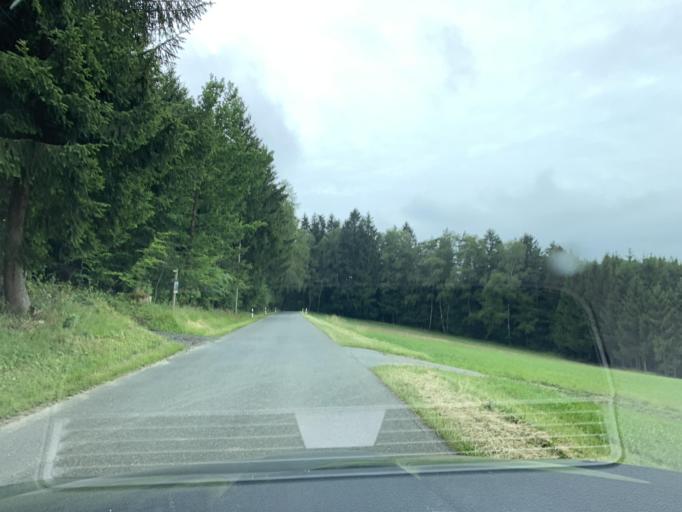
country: DE
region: Bavaria
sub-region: Upper Palatinate
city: Winklarn
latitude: 49.4232
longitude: 12.4544
